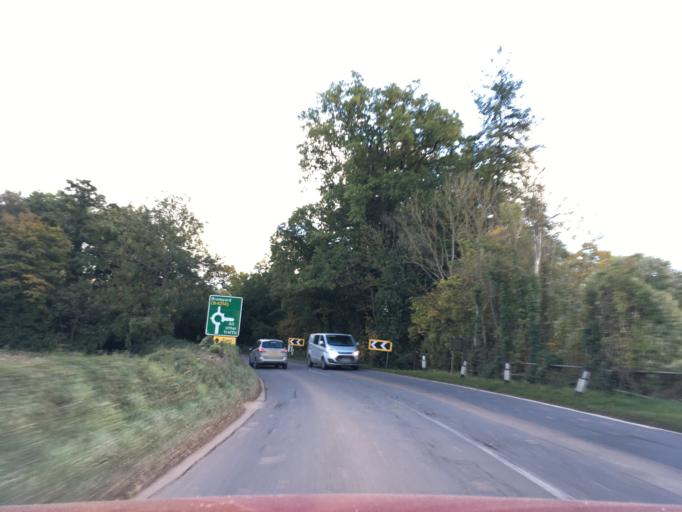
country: GB
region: England
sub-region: Herefordshire
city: Ledbury
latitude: 52.0451
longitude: -2.4387
